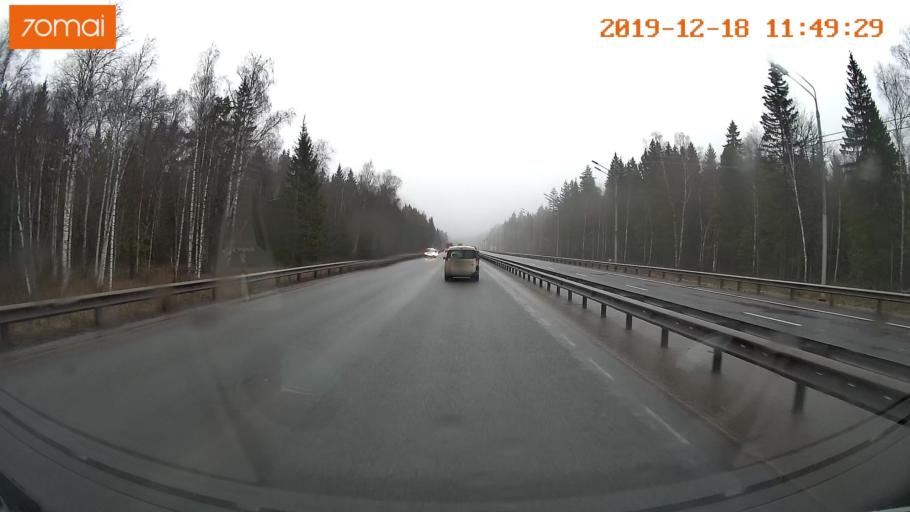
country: RU
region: Moskovskaya
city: Yershovo
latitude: 55.7780
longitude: 36.9120
